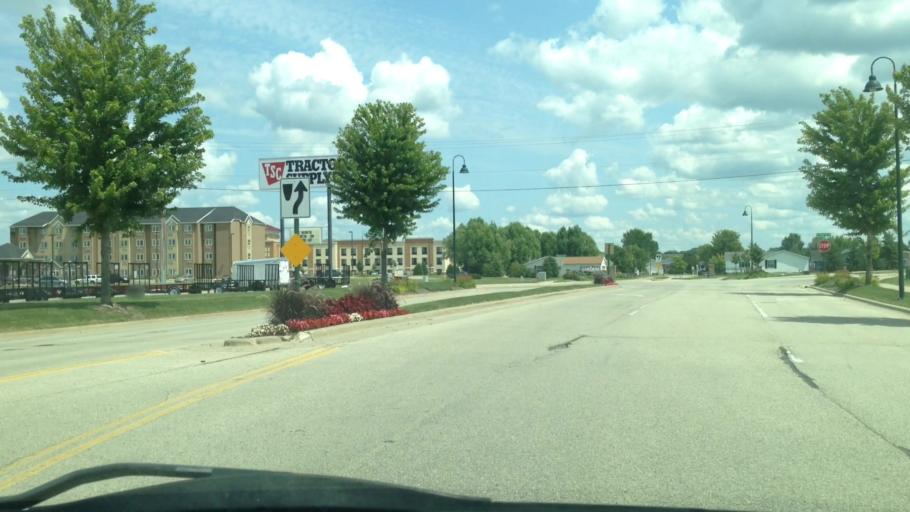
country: US
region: Minnesota
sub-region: Olmsted County
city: Rochester
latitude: 43.9610
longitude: -92.4595
